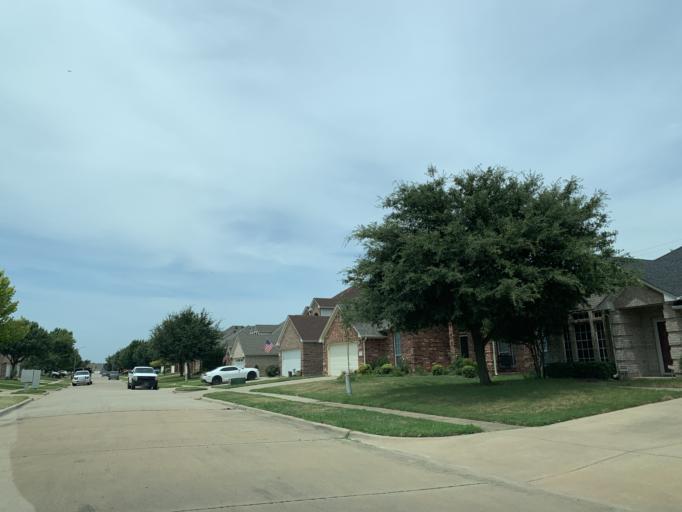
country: US
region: Texas
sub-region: Dallas County
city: Grand Prairie
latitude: 32.6604
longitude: -97.0184
